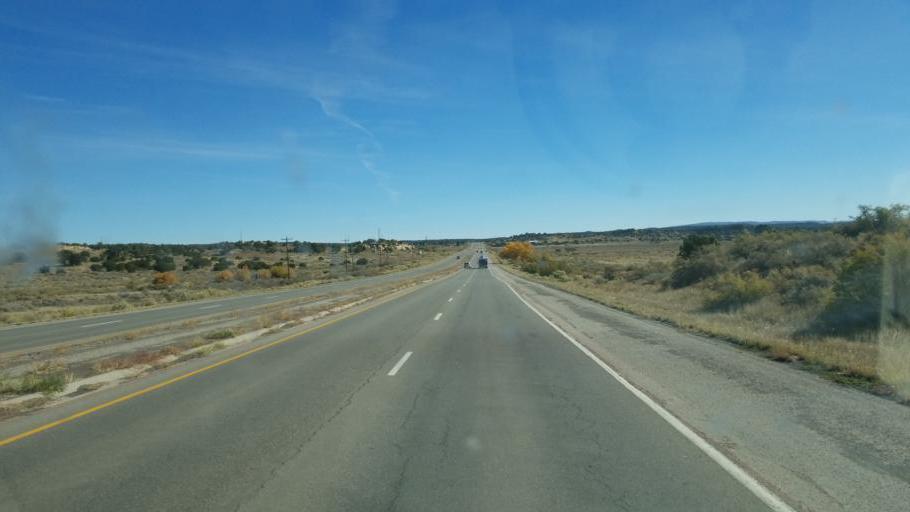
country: US
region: Arizona
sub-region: Apache County
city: Window Rock
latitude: 35.6286
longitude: -108.9259
